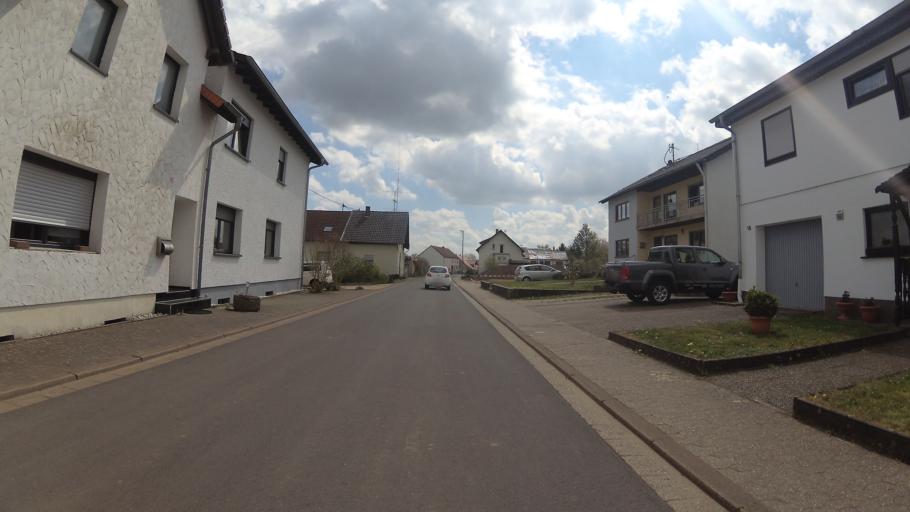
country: DE
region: Saarland
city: Wadern
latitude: 49.5576
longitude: 6.8607
